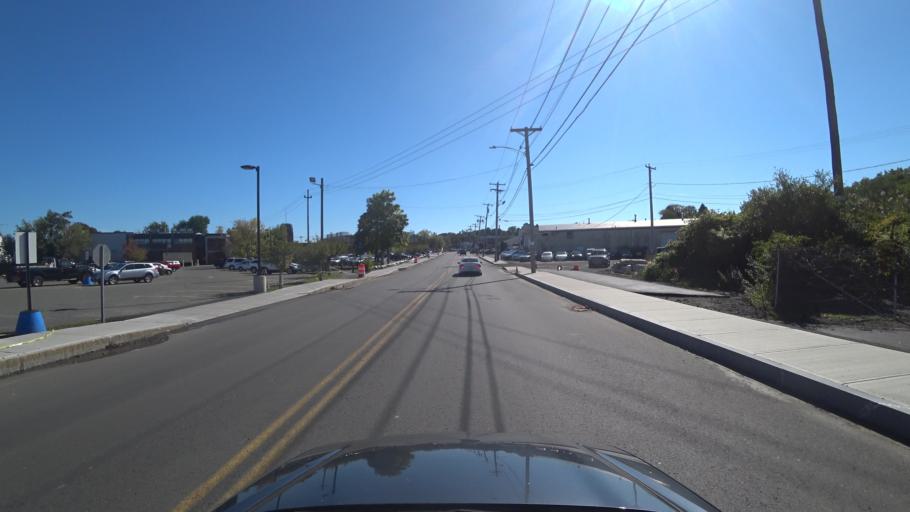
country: US
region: Massachusetts
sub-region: Essex County
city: Salem
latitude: 42.5033
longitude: -70.8961
